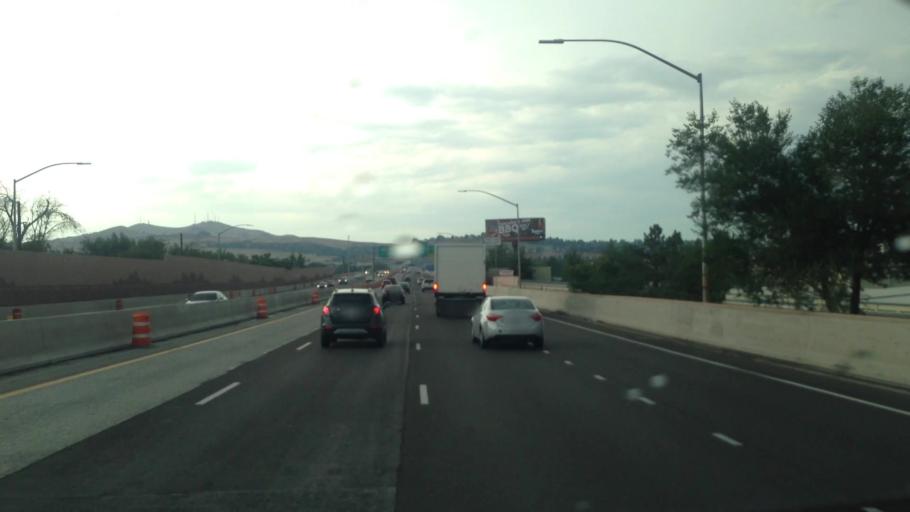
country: US
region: Nevada
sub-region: Washoe County
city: Reno
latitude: 39.5408
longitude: -119.7878
